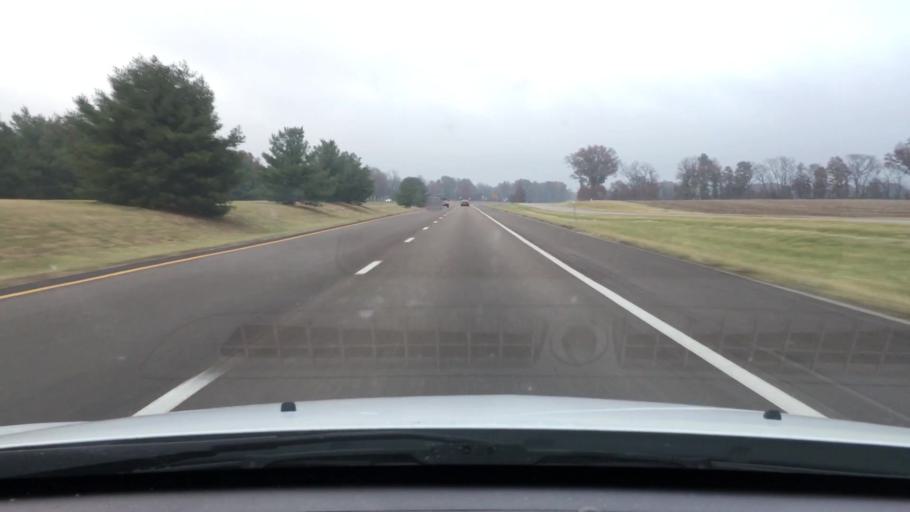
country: US
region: Missouri
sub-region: Callaway County
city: Fulton
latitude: 38.9549
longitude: -91.9359
